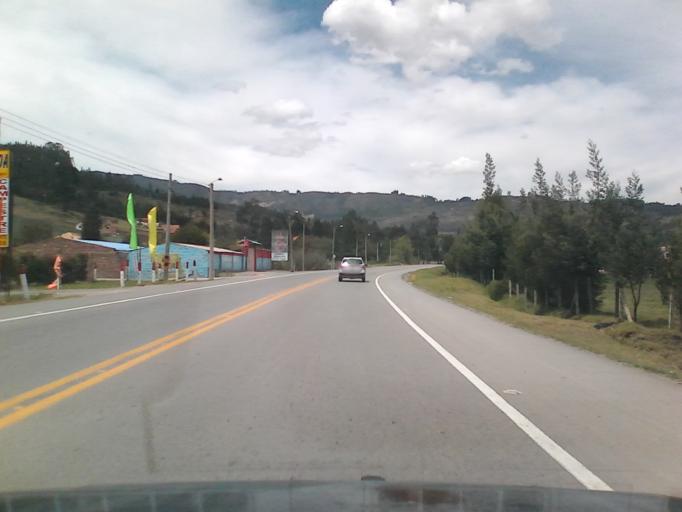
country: CO
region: Boyaca
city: Tibasosa
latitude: 5.7440
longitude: -72.9818
